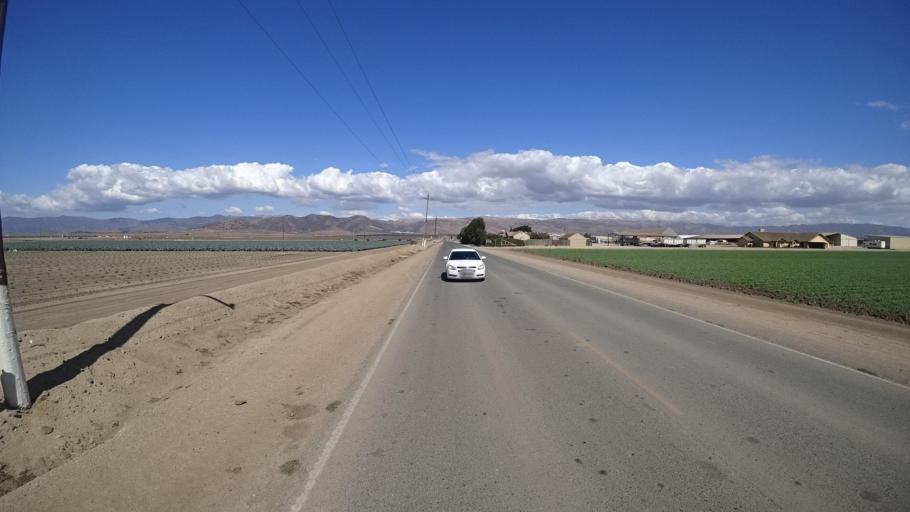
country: US
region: California
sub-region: Monterey County
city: Gonzales
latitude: 36.5376
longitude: -121.4648
